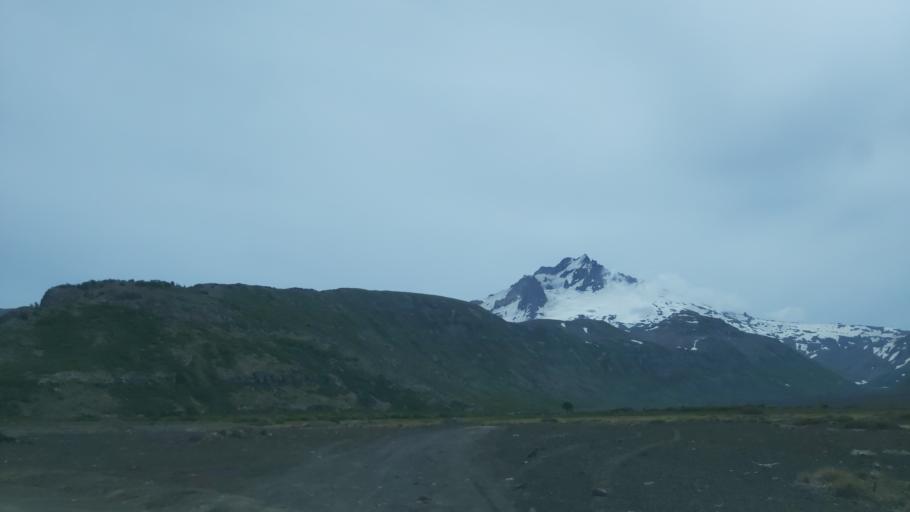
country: AR
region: Neuquen
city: Andacollo
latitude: -37.4616
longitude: -71.3141
